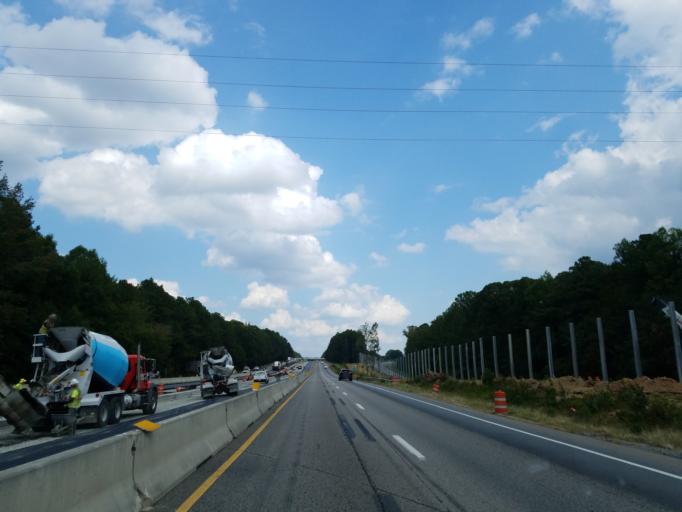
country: US
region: Georgia
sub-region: Gwinnett County
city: Buford
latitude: 34.0603
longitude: -83.9558
